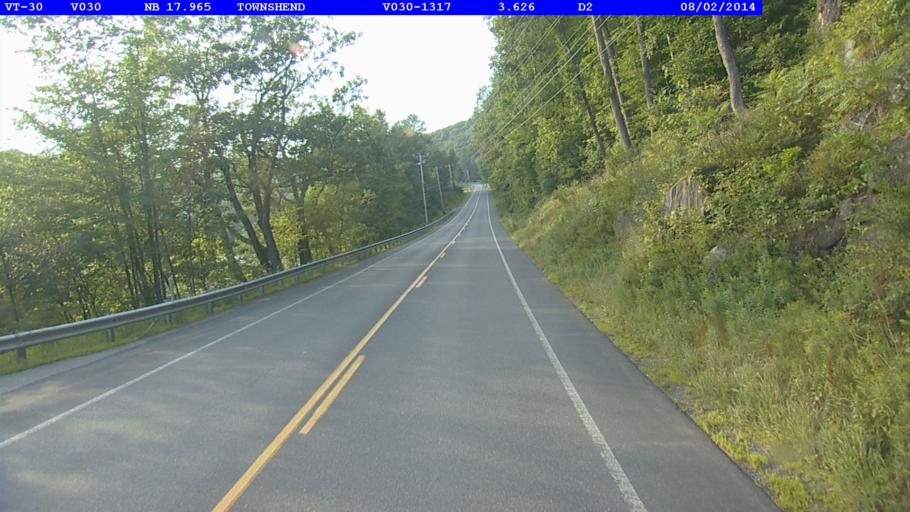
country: US
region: Vermont
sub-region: Windham County
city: Newfane
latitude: 43.0488
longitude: -72.6959
